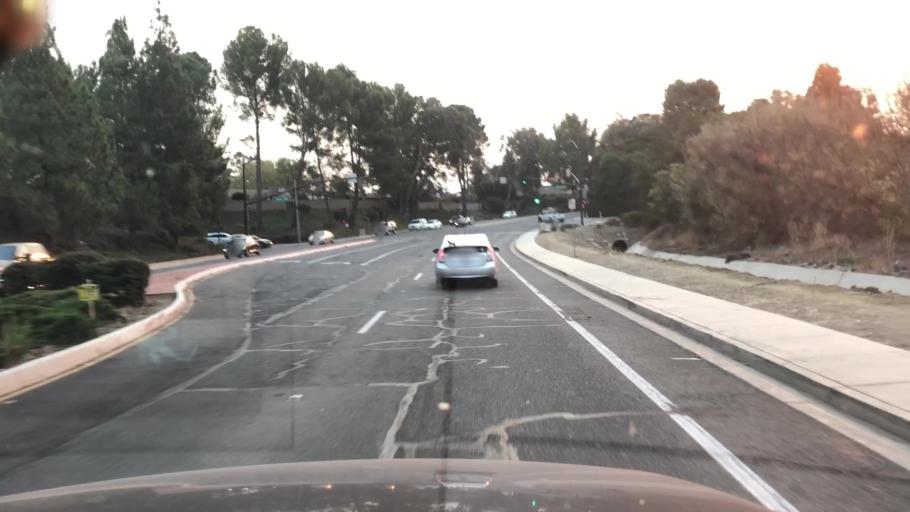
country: US
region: California
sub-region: Ventura County
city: Thousand Oaks
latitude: 34.2069
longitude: -118.8860
